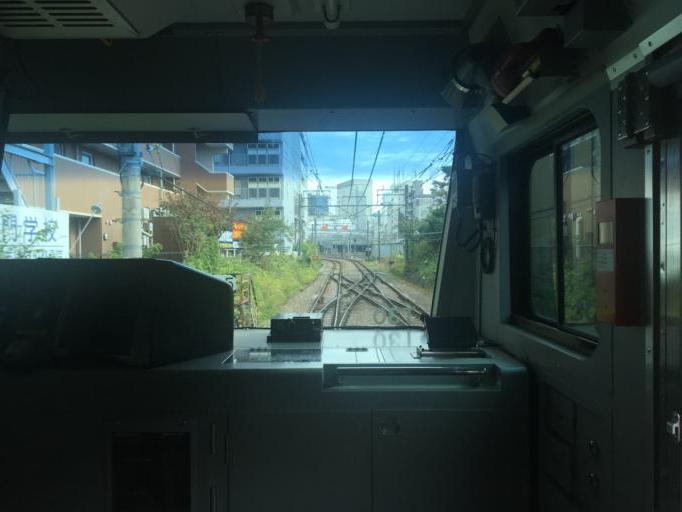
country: JP
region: Tokyo
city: Hino
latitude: 35.6988
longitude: 139.4090
